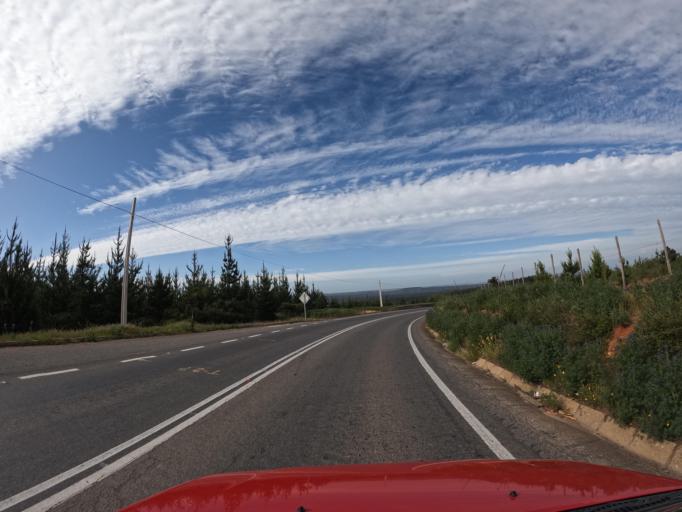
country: CL
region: O'Higgins
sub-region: Provincia de Colchagua
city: Santa Cruz
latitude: -34.3037
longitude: -71.8334
